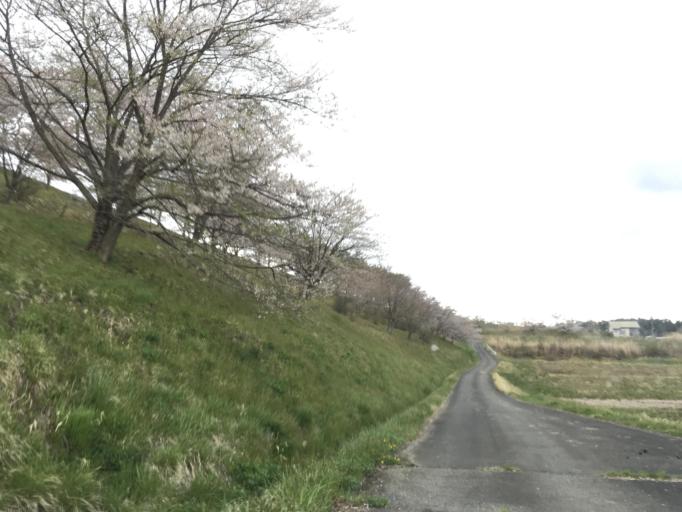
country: JP
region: Iwate
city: Ichinoseki
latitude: 38.8523
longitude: 141.3280
